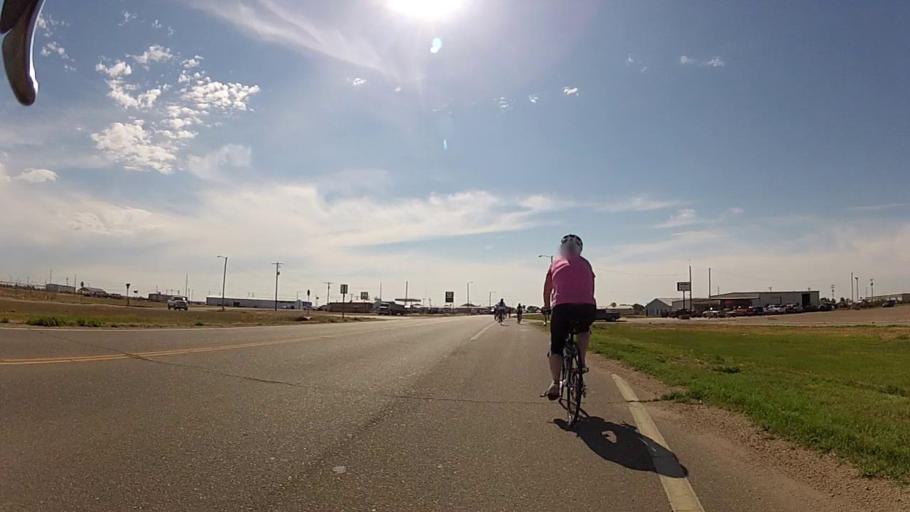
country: US
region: Kansas
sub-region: Grant County
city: Ulysses
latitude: 37.5761
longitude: -101.3495
